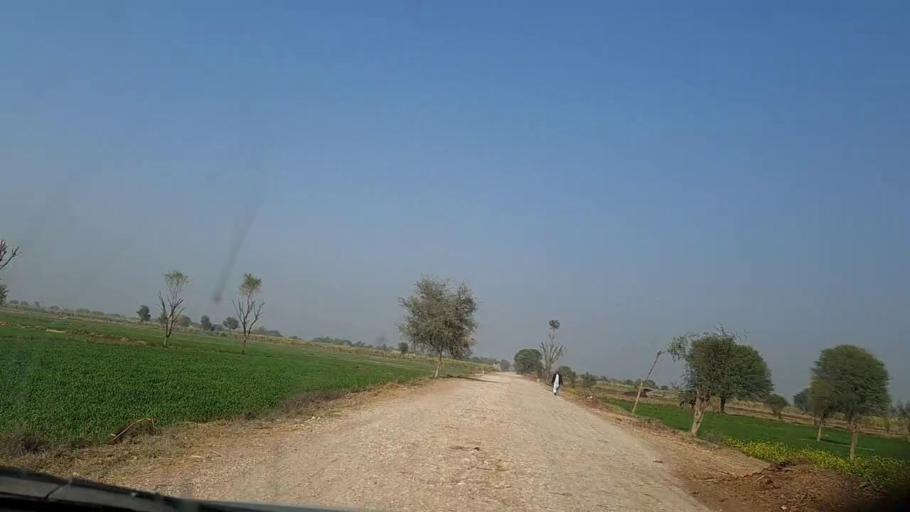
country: PK
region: Sindh
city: Moro
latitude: 26.7793
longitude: 67.9353
